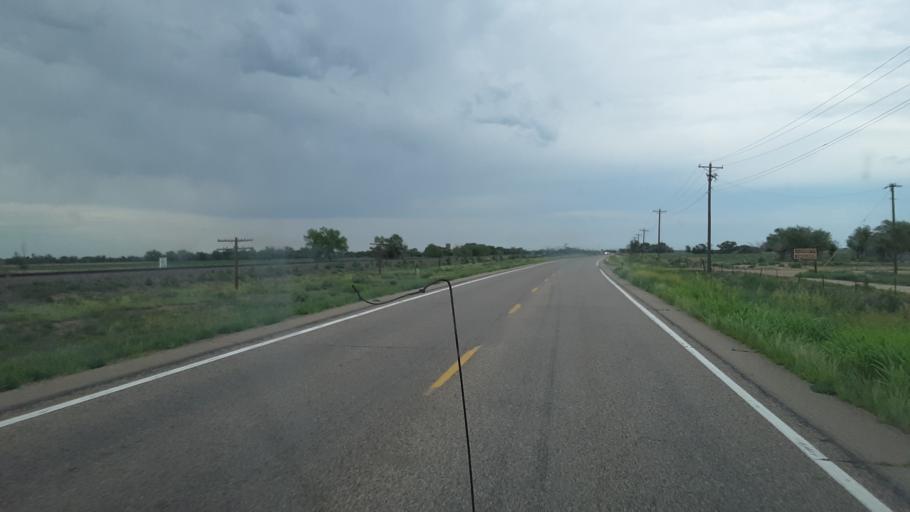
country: US
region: Colorado
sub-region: Crowley County
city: Ordway
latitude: 38.2015
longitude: -103.8236
